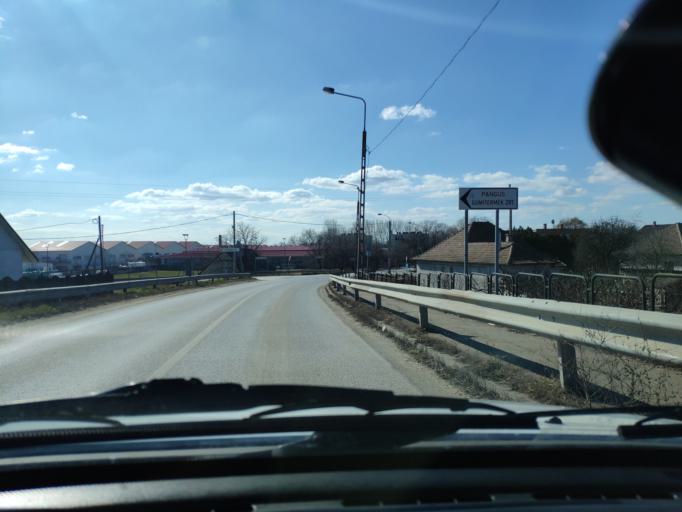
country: HU
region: Pest
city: Ecser
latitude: 47.4392
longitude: 19.3182
